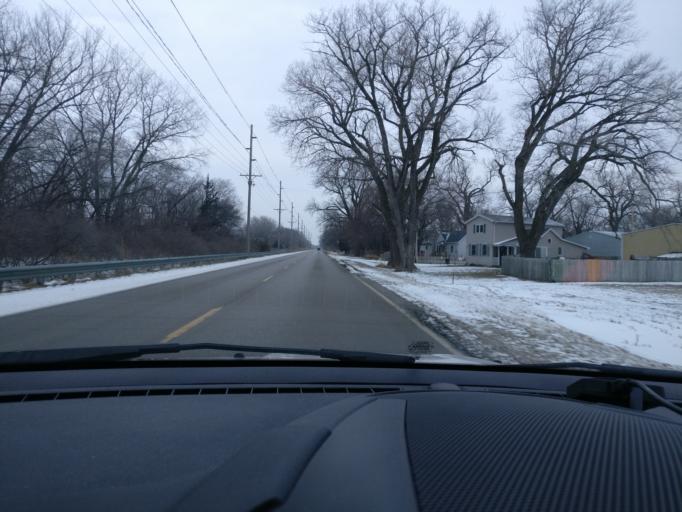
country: US
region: Nebraska
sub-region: Dodge County
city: Fremont
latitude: 41.4406
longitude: -96.5296
